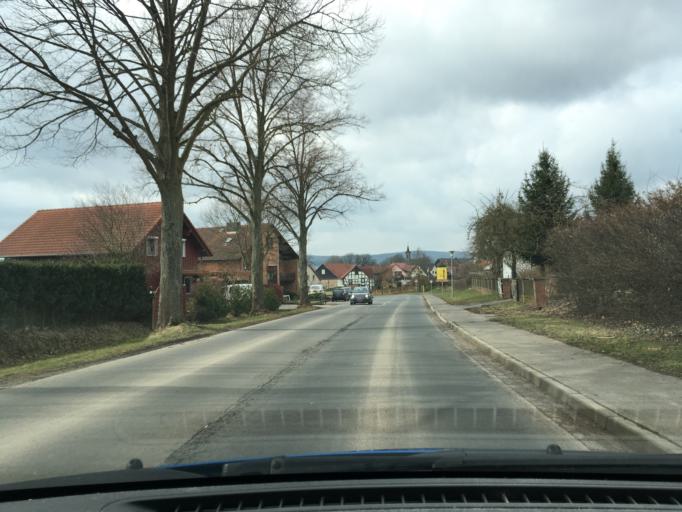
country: DE
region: Lower Saxony
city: Dransfeld
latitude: 51.5186
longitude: 9.7313
